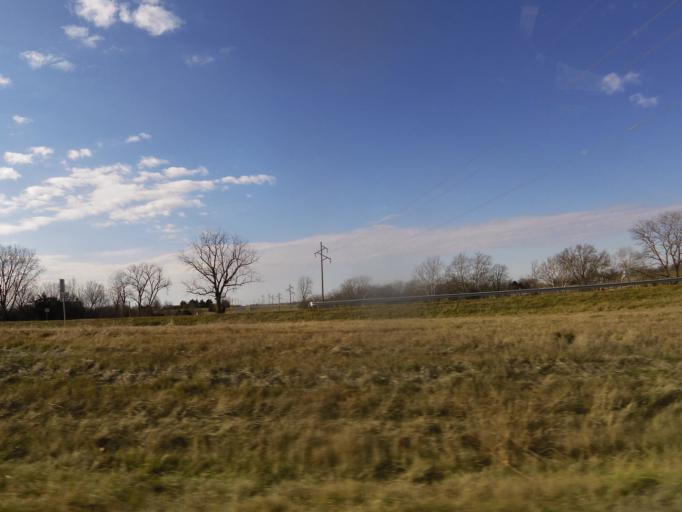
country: US
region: Missouri
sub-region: Marion County
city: Hannibal
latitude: 39.6711
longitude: -91.4150
